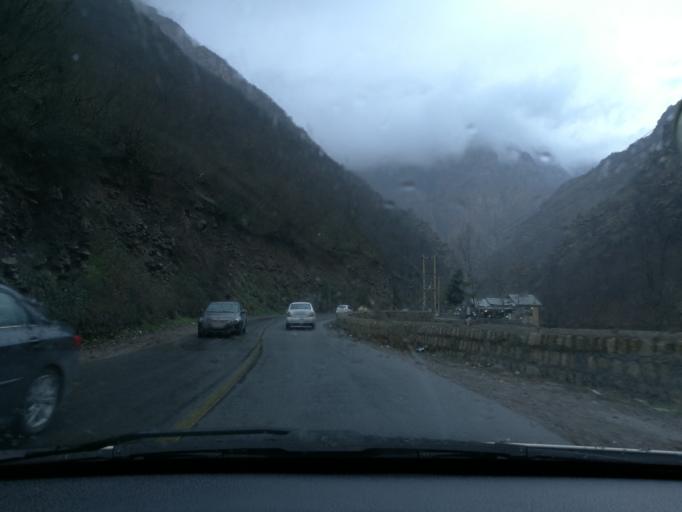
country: IR
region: Mazandaran
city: Chalus
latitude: 36.2667
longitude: 51.2564
